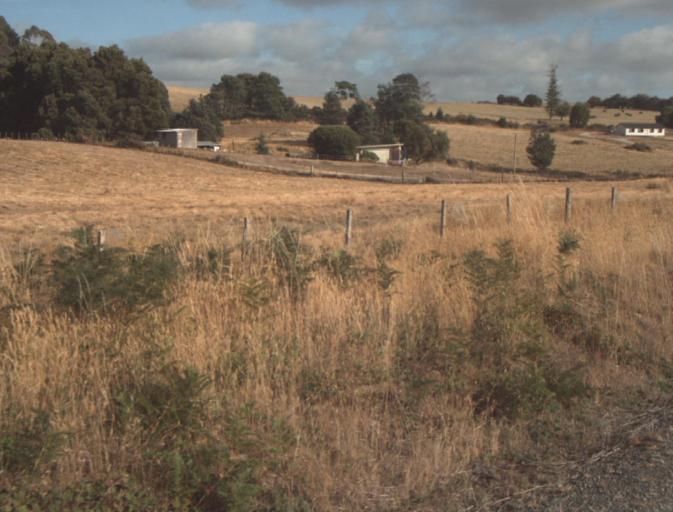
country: AU
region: Tasmania
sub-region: Launceston
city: Mayfield
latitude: -41.1894
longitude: 147.2216
